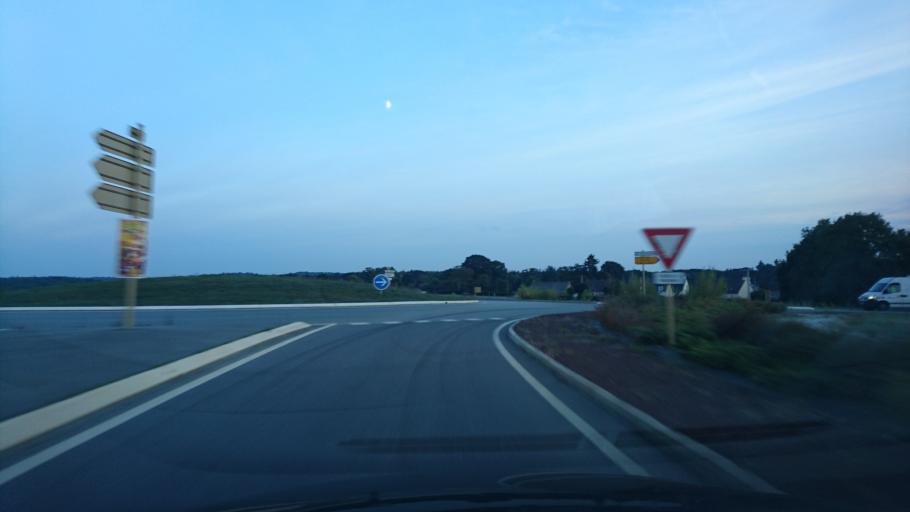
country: FR
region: Brittany
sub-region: Departement d'Ille-et-Vilaine
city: Guignen
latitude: 47.9210
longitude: -1.8519
